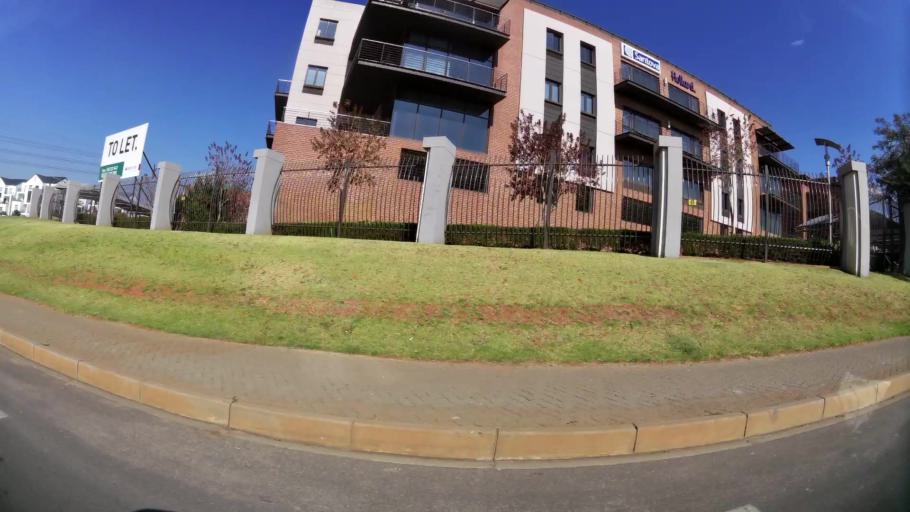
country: ZA
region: Gauteng
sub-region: City of Johannesburg Metropolitan Municipality
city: Modderfontein
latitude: -26.1199
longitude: 28.1455
